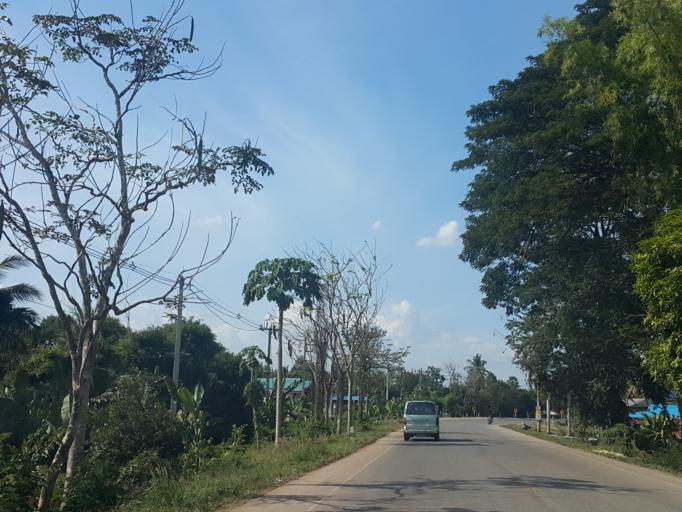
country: TH
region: Sukhothai
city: Sawankhalok
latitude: 17.2574
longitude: 99.8382
